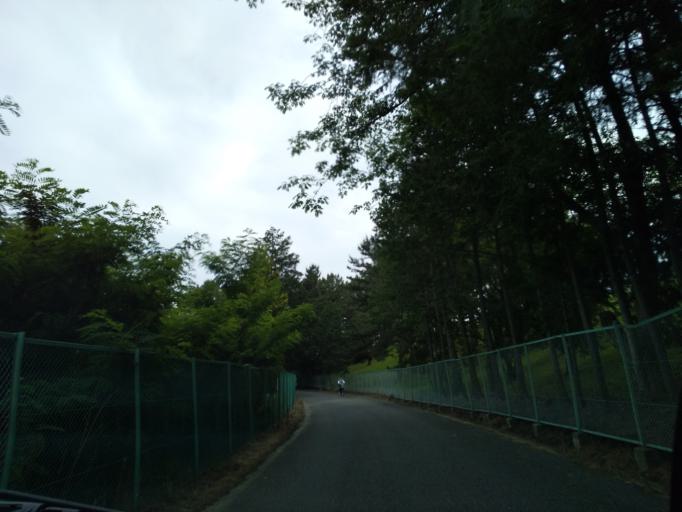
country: JP
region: Kanagawa
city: Atsugi
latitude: 35.4804
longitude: 139.3263
